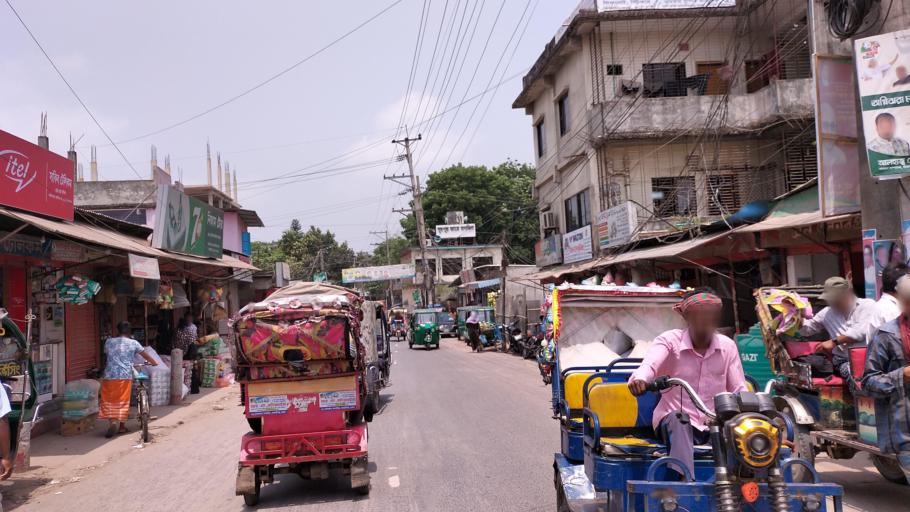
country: BD
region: Dhaka
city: Azimpur
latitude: 23.7324
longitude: 90.2732
